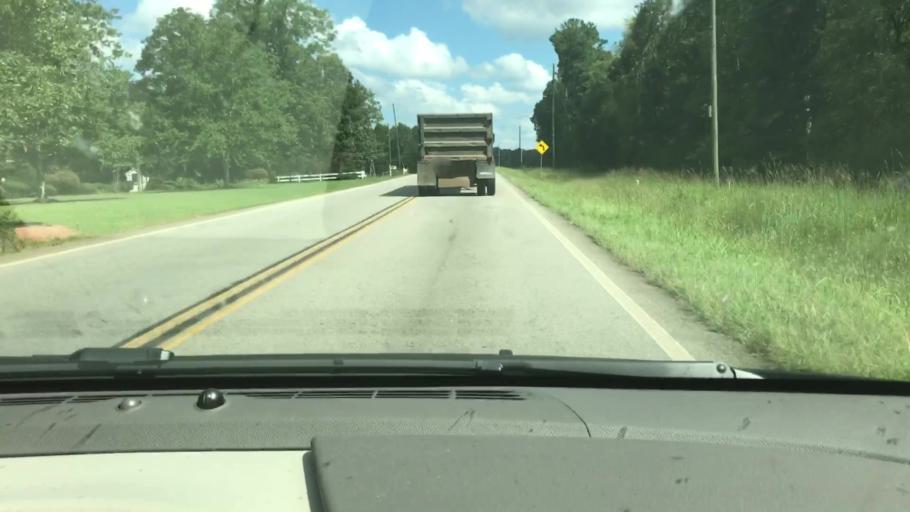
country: US
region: Alabama
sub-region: Chambers County
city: Valley
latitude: 32.8465
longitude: -85.0355
